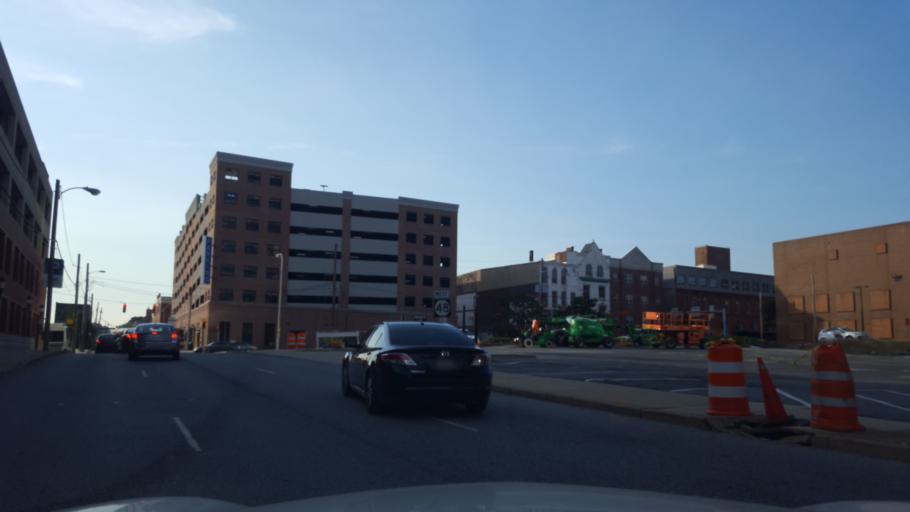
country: US
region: Delaware
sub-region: New Castle County
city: Wilmington
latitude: 39.7381
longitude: -75.5507
